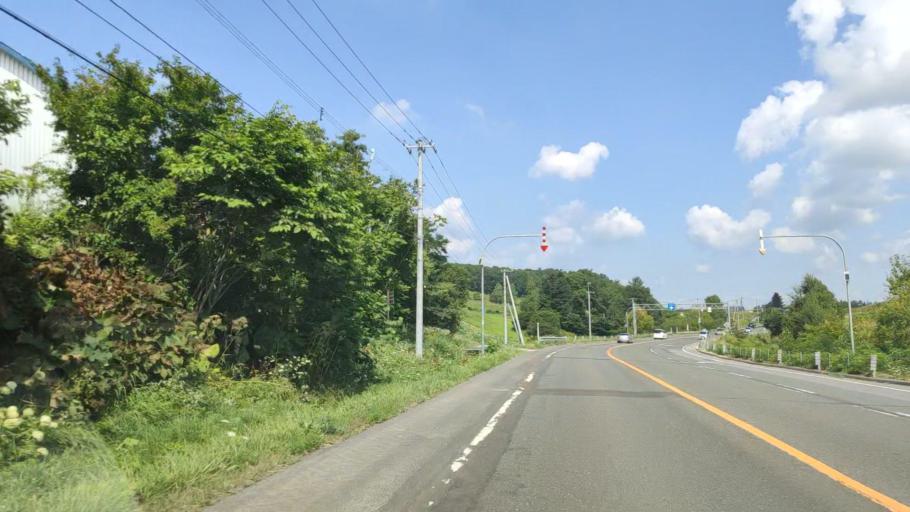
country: JP
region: Hokkaido
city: Shimo-furano
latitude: 43.5364
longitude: 142.4400
